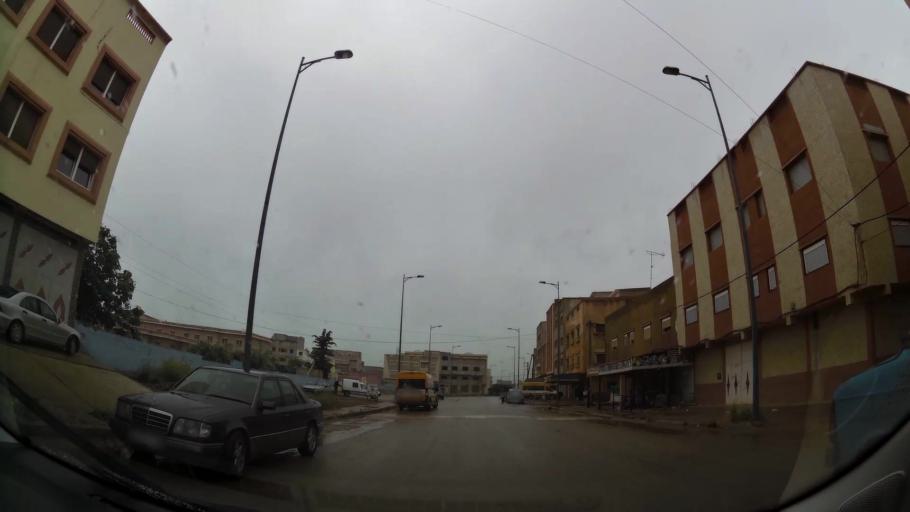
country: MA
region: Oriental
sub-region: Nador
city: Boudinar
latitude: 35.1134
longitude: -3.6429
